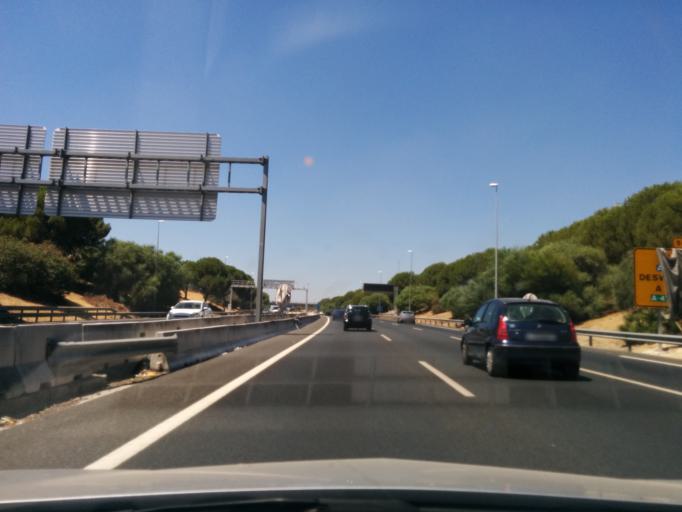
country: ES
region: Andalusia
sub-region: Provincia de Sevilla
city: Bormujos
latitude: 37.3825
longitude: -6.0678
